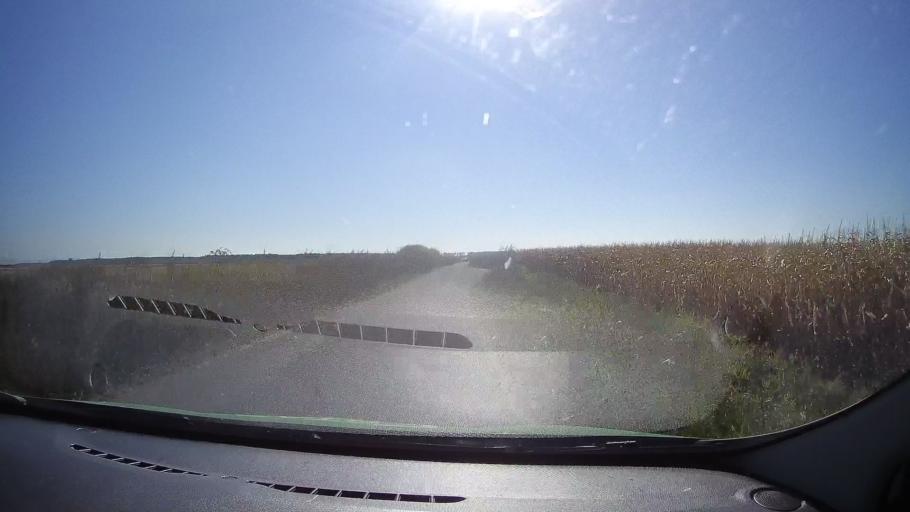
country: RO
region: Satu Mare
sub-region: Comuna Doba
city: Doba
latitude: 47.7315
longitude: 22.7241
